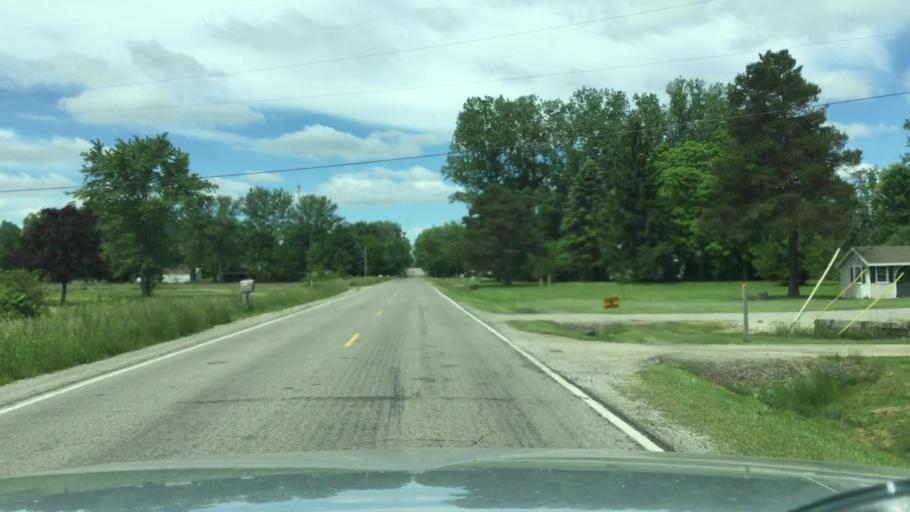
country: US
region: Michigan
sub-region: Genesee County
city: Clio
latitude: 43.1919
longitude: -83.7592
